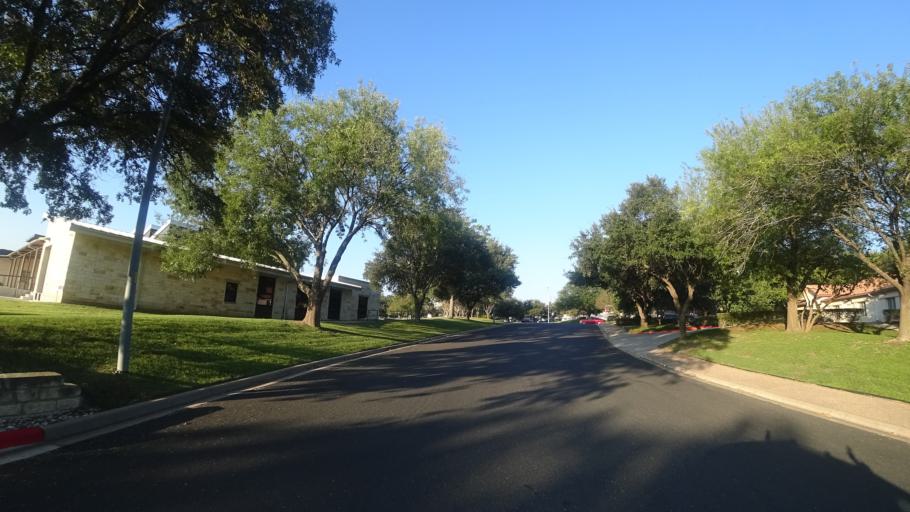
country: US
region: Texas
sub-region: Travis County
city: Austin
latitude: 30.3326
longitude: -97.6791
